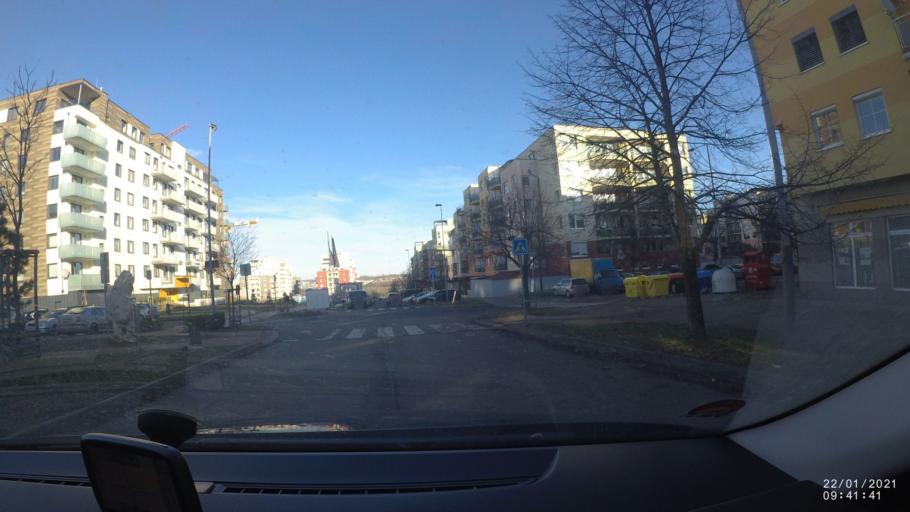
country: CZ
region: Praha
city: Branik
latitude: 50.0289
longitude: 14.3637
